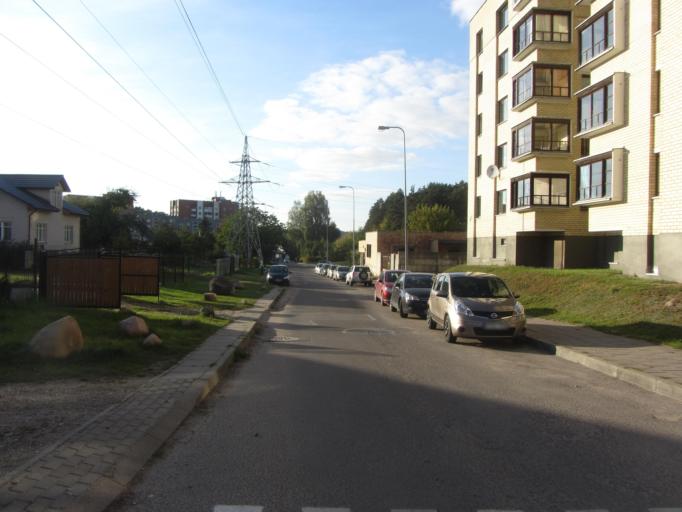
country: LT
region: Vilnius County
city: Lazdynai
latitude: 54.6409
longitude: 25.2101
